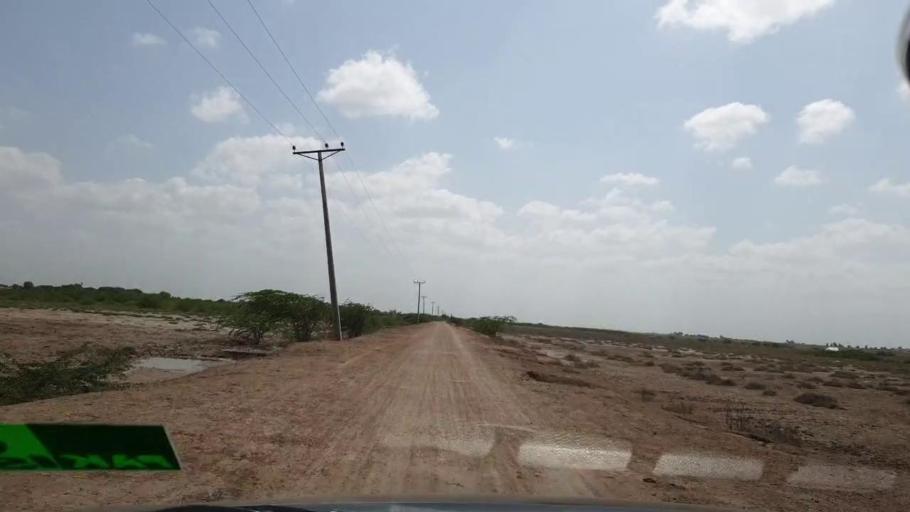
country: PK
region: Sindh
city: Kadhan
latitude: 24.6044
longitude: 69.1852
